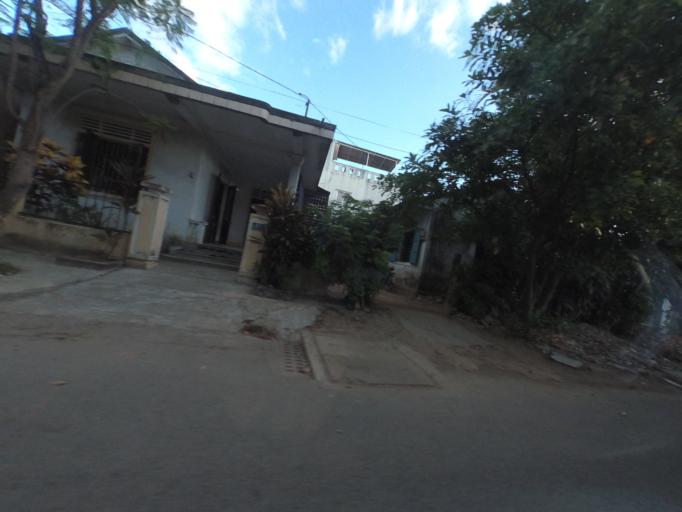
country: VN
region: Thua Thien-Hue
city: Hue
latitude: 16.4885
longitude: 107.5887
